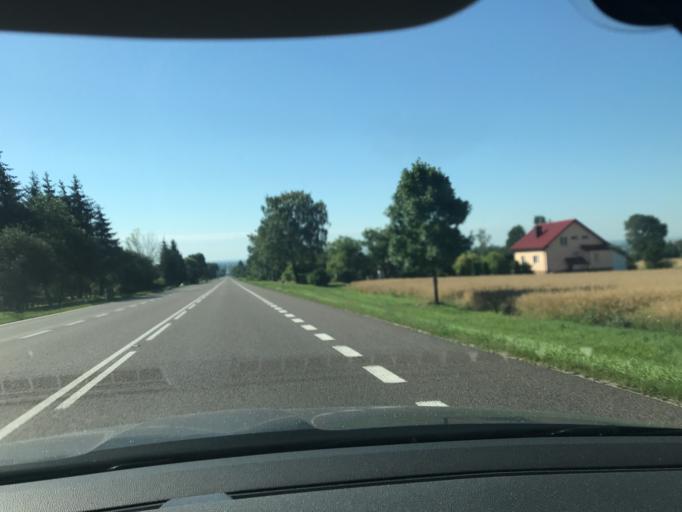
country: PL
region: Lublin Voivodeship
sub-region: Powiat zamojski
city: Stary Zamosc
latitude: 50.8419
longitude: 23.1712
